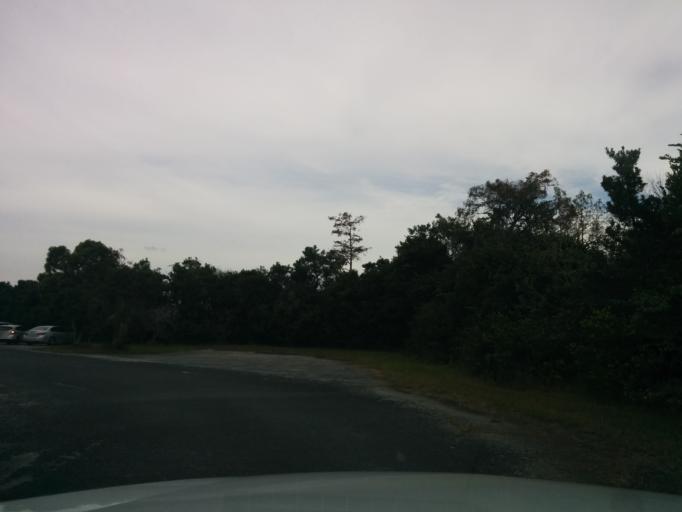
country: US
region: Florida
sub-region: Miami-Dade County
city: Florida City
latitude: 25.4402
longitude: -80.7827
